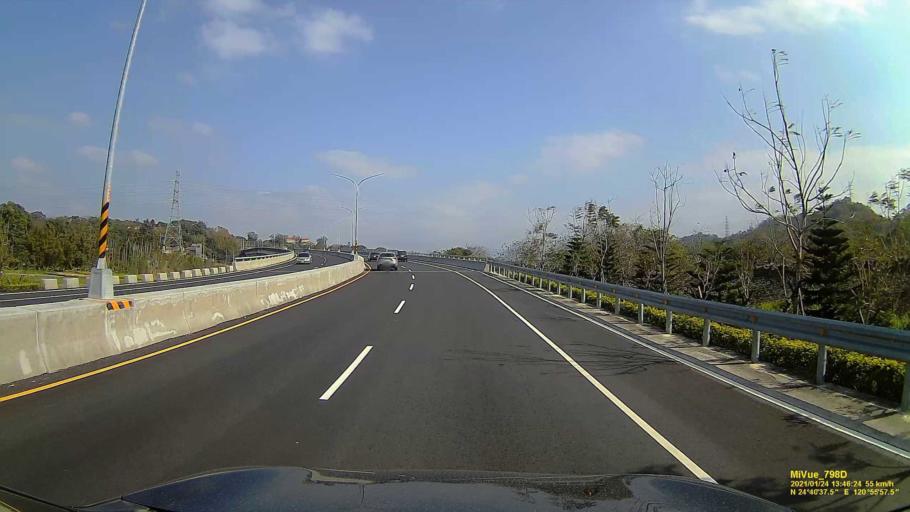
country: TW
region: Taiwan
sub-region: Hsinchu
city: Hsinchu
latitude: 24.6772
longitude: 120.9325
